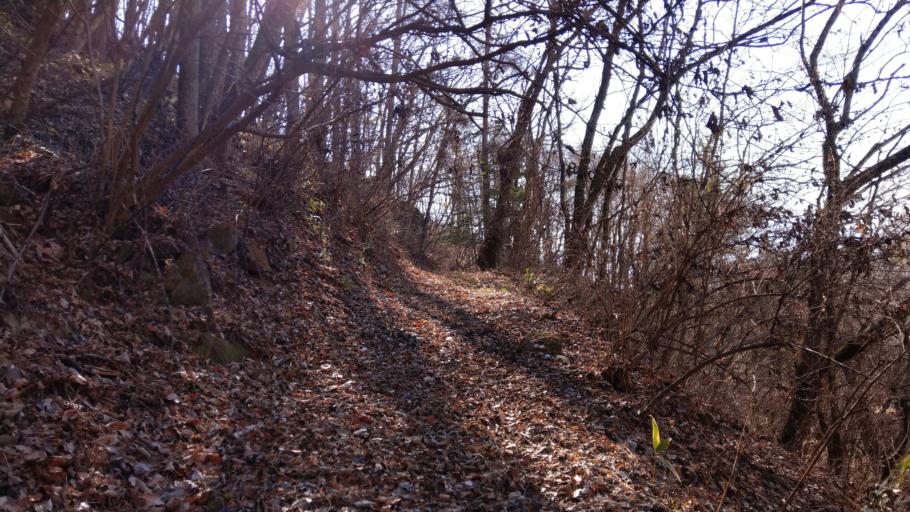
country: JP
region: Nagano
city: Komoro
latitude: 36.3627
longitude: 138.4444
